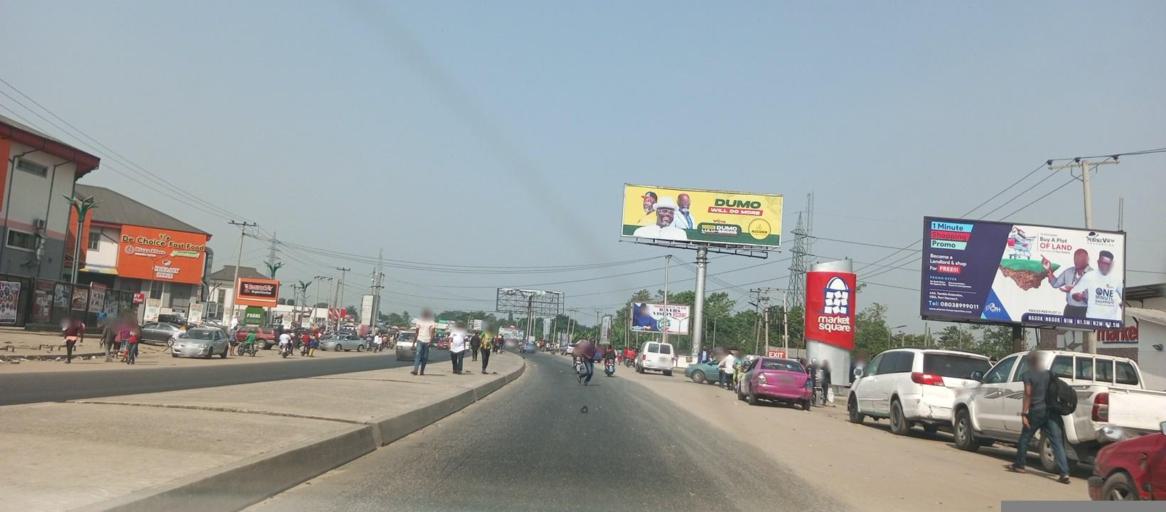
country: NG
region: Rivers
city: Emuoha
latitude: 4.8979
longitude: 6.9085
